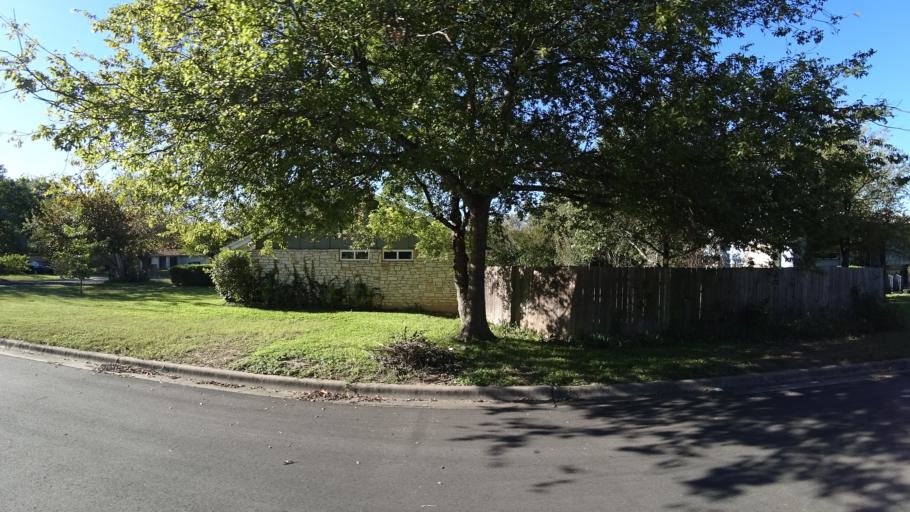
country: US
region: Texas
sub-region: Travis County
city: Austin
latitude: 30.3073
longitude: -97.6634
